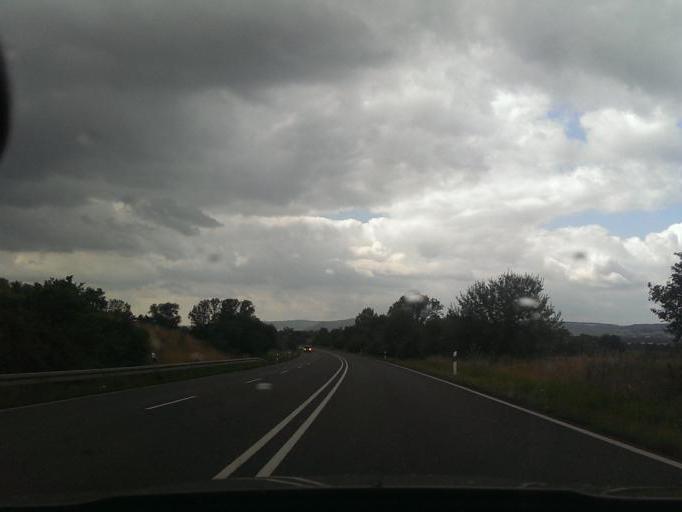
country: DE
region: Lower Saxony
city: Bevern
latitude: 51.8485
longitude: 9.4973
